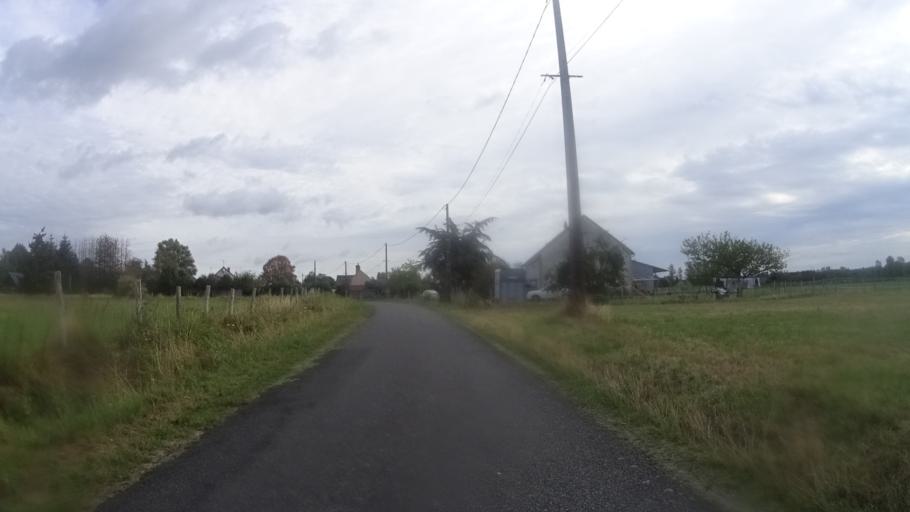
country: FR
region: Centre
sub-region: Departement du Loiret
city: Vitry-aux-Loges
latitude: 47.9885
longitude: 2.2081
